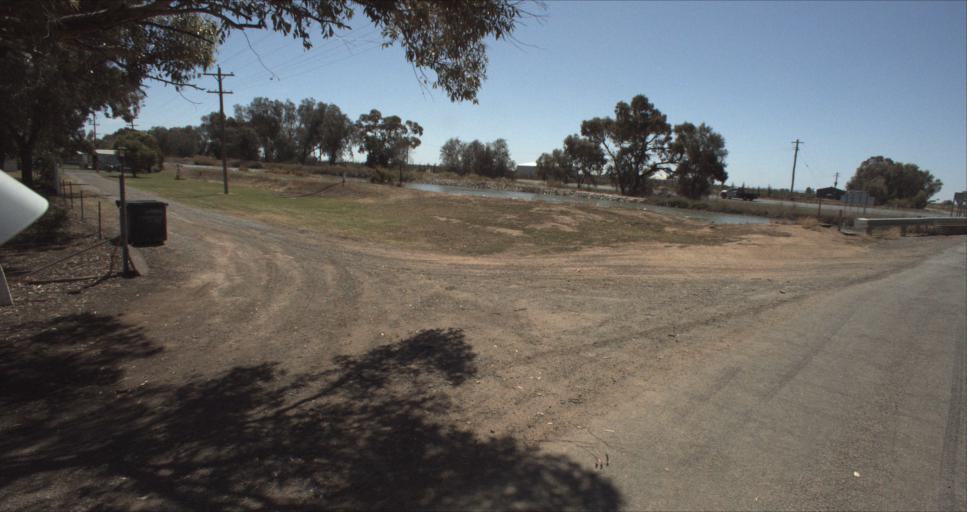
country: AU
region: New South Wales
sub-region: Leeton
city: Leeton
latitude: -34.5247
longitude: 146.3458
